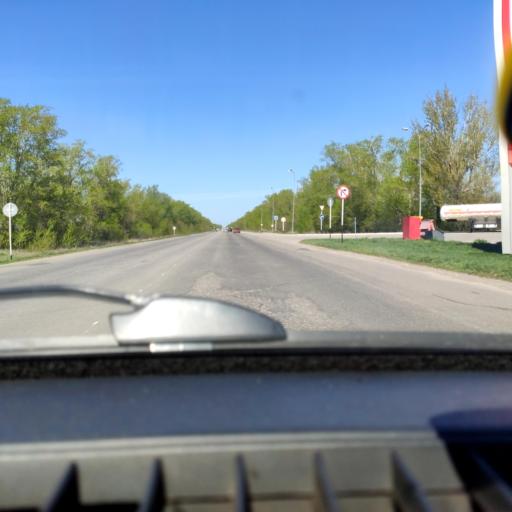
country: RU
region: Samara
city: Tol'yatti
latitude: 53.5962
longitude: 49.4078
